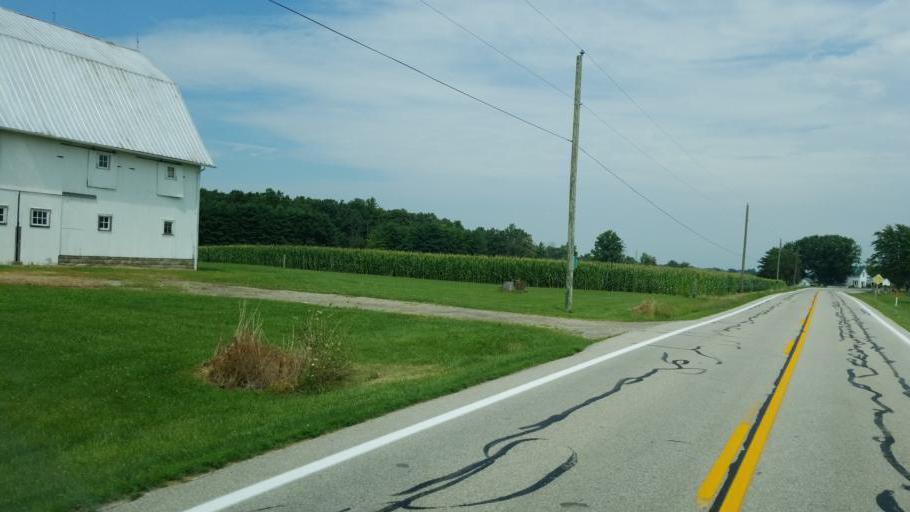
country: US
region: Ohio
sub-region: Union County
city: Richwood
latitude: 40.3516
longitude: -83.3607
